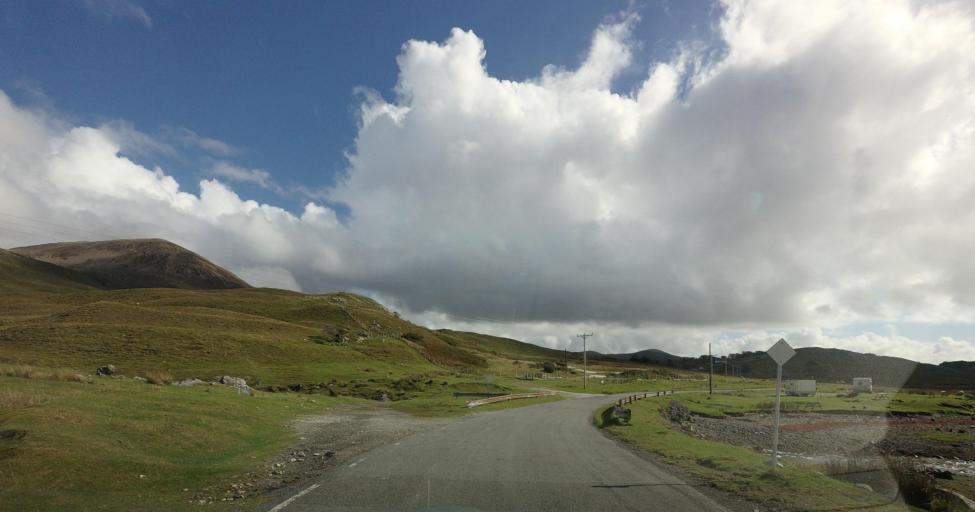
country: GB
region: Scotland
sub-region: Highland
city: Portree
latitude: 57.2186
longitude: -6.0246
